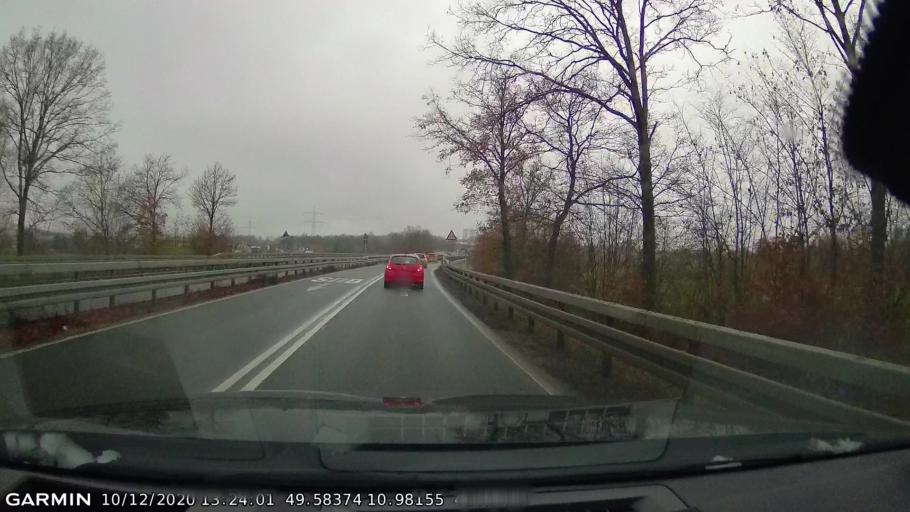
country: DE
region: Bavaria
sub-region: Regierungsbezirk Mittelfranken
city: Erlangen
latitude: 49.5837
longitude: 10.9815
